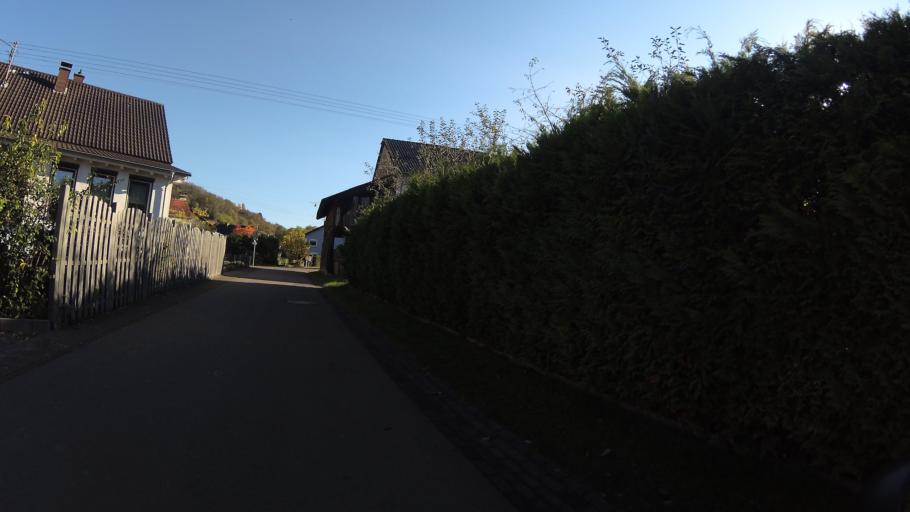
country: DE
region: Saarland
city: Losheim
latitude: 49.4722
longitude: 6.7239
